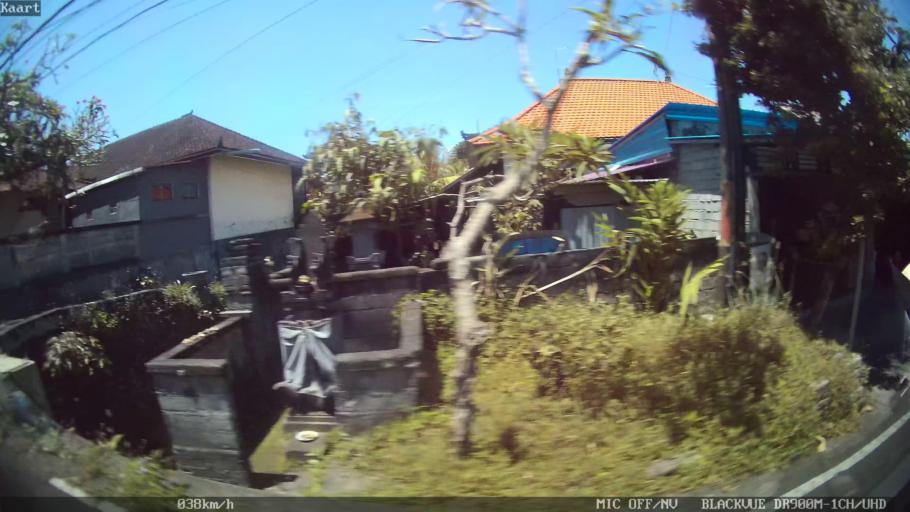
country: ID
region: Bali
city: Klungkung
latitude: -8.5722
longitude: 115.3359
